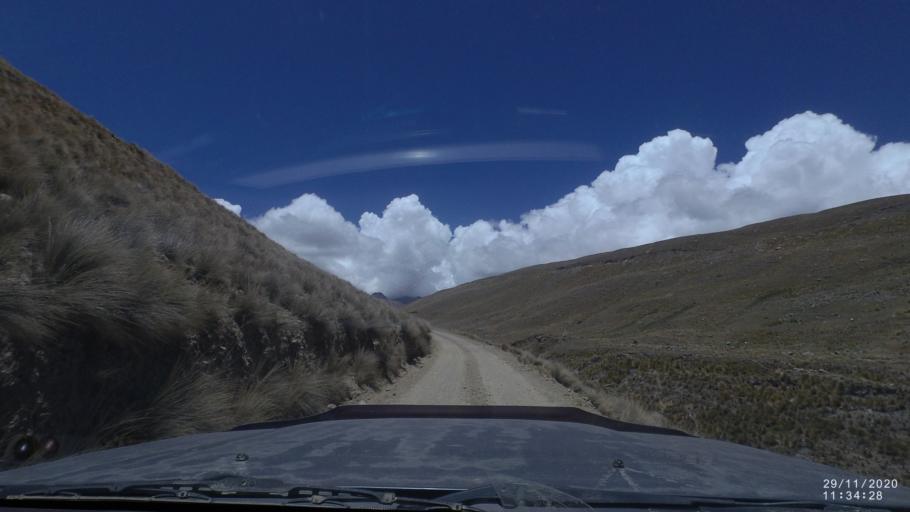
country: BO
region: Cochabamba
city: Cochabamba
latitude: -17.1881
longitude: -66.2207
